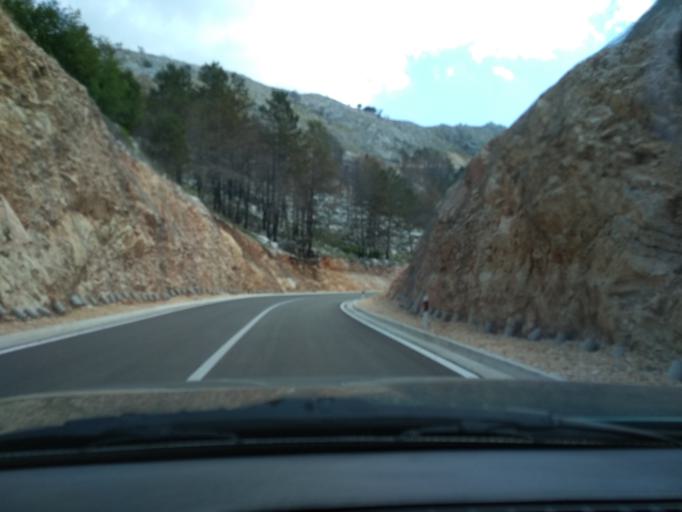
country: ME
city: Dobrota
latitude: 42.4375
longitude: 18.8386
